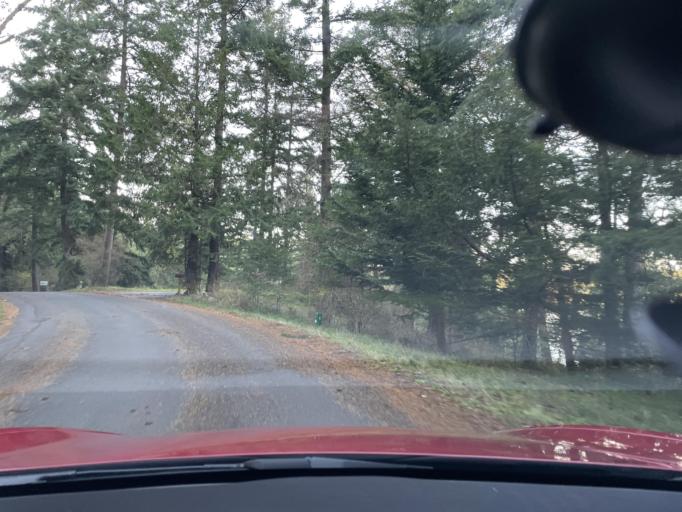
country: US
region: Washington
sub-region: San Juan County
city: Friday Harbor
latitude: 48.6001
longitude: -123.1508
